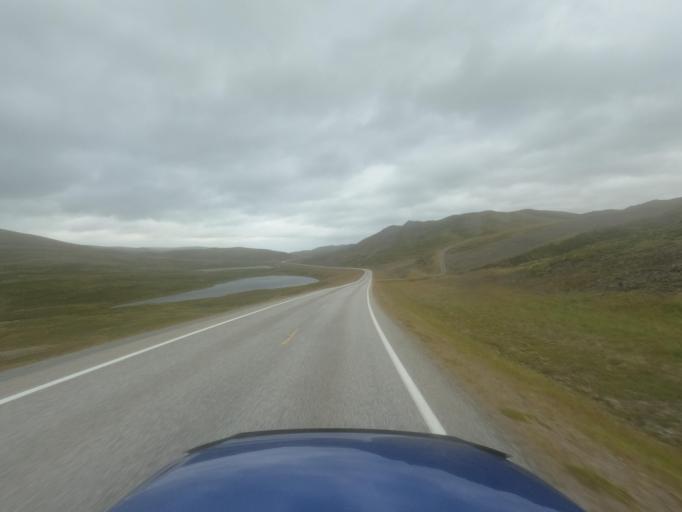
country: NO
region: Finnmark Fylke
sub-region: Nordkapp
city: Honningsvag
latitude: 71.0811
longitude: 25.7721
